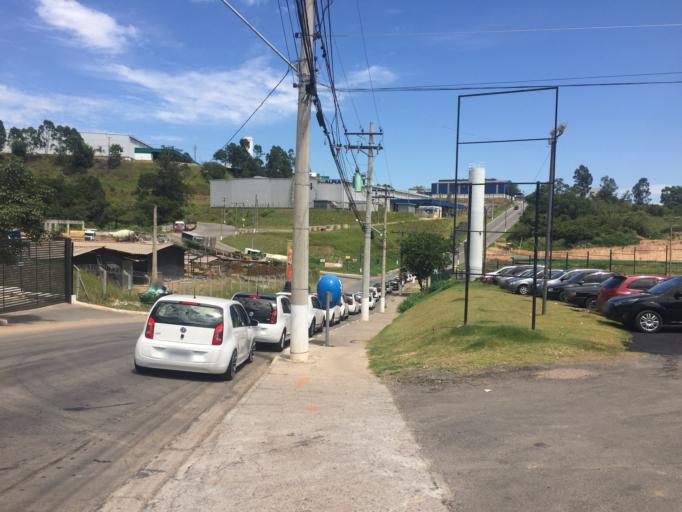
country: BR
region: Sao Paulo
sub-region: Louveira
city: Louveira
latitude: -23.0922
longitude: -46.9617
